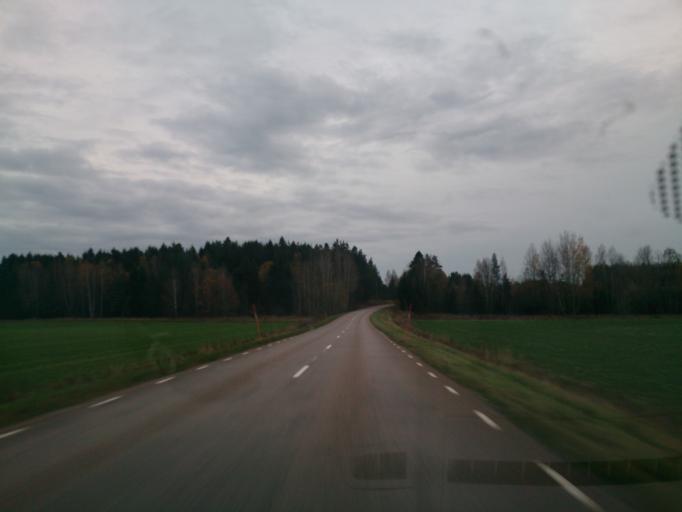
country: SE
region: OEstergoetland
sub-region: Linkopings Kommun
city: Linghem
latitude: 58.4610
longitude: 15.8839
